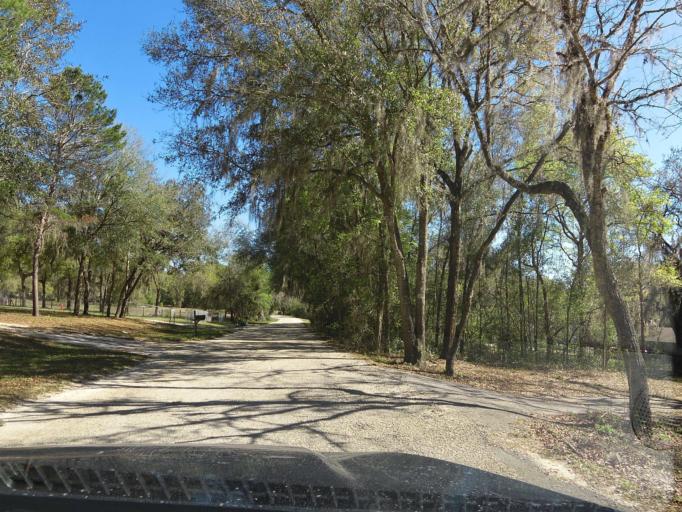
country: US
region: Florida
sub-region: Clay County
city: Keystone Heights
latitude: 29.8125
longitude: -82.0462
